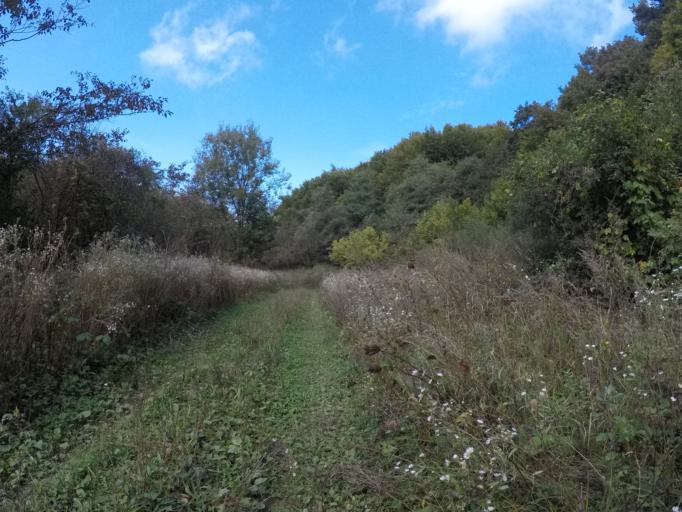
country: SK
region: Presovsky
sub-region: Okres Presov
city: Presov
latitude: 48.9327
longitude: 21.1648
